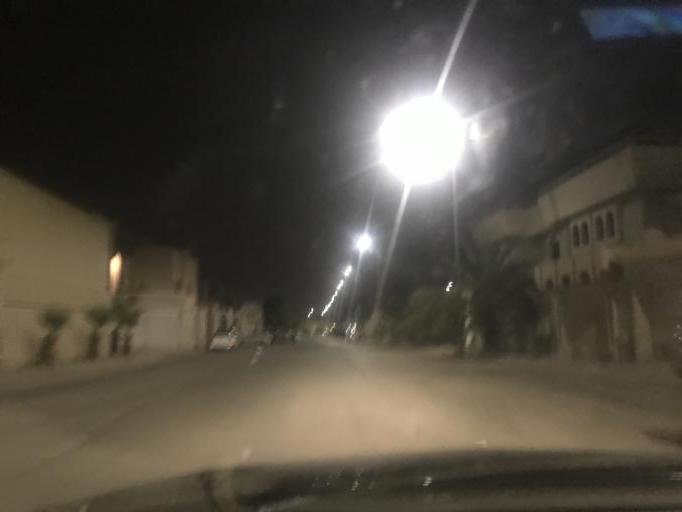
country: SA
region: Ar Riyad
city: Riyadh
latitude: 24.7368
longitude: 46.7692
